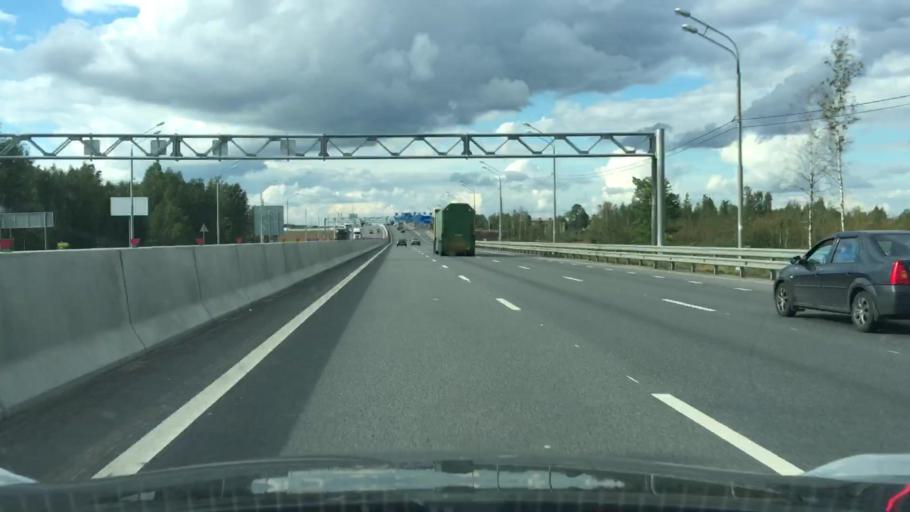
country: RU
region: Tverskaya
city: Tver
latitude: 56.8276
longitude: 35.8102
